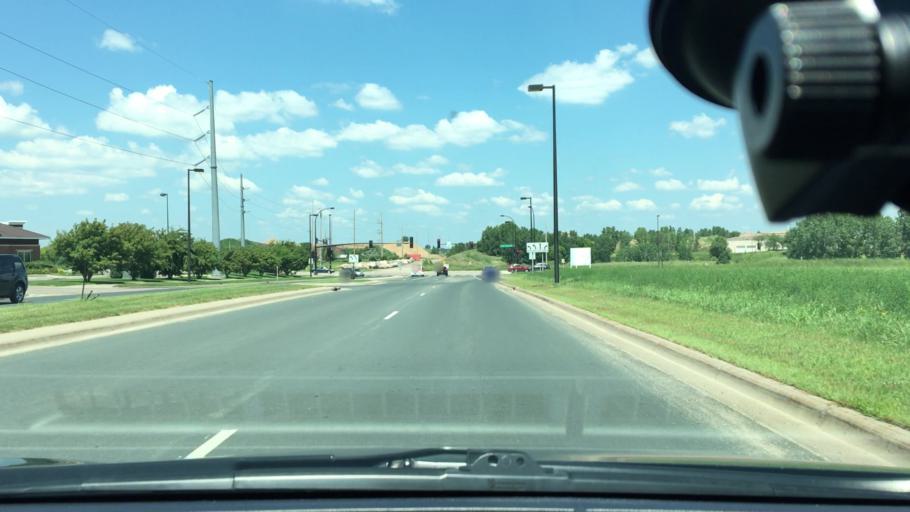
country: US
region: Minnesota
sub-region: Hennepin County
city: Osseo
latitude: 45.0928
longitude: -93.4215
